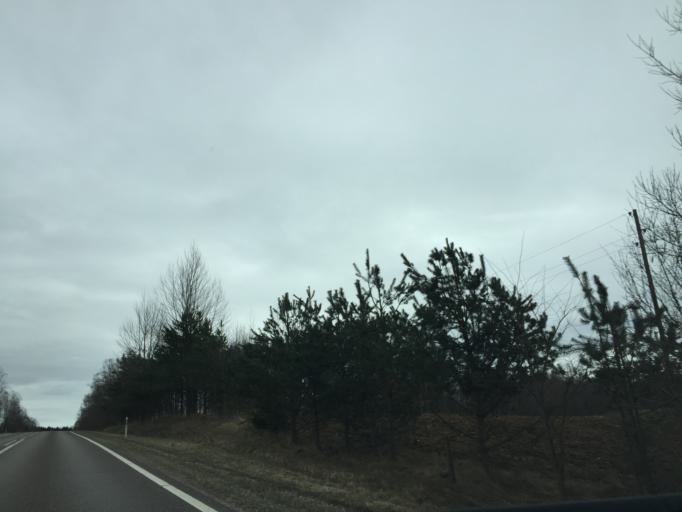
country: LV
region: Kraslavas Rajons
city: Kraslava
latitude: 55.9105
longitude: 27.0815
